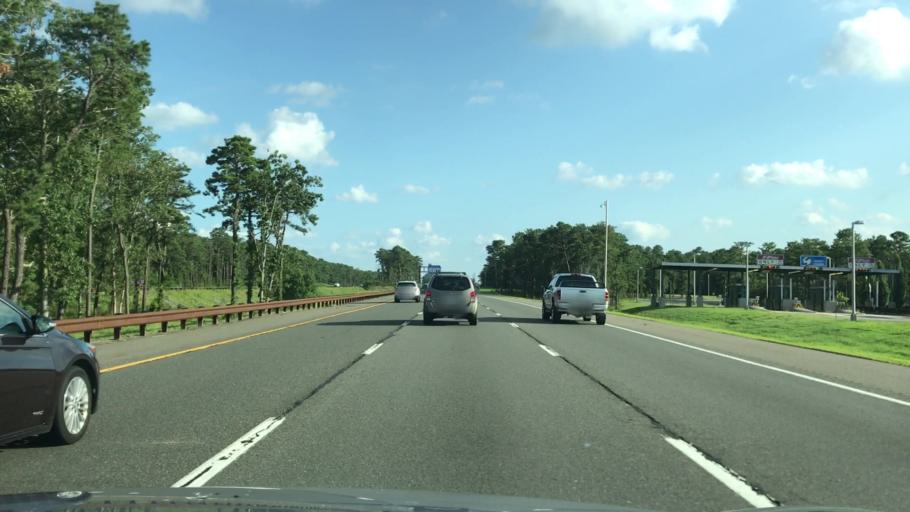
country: US
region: New Jersey
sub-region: Ocean County
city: South Toms River
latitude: 39.9069
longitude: -74.2125
